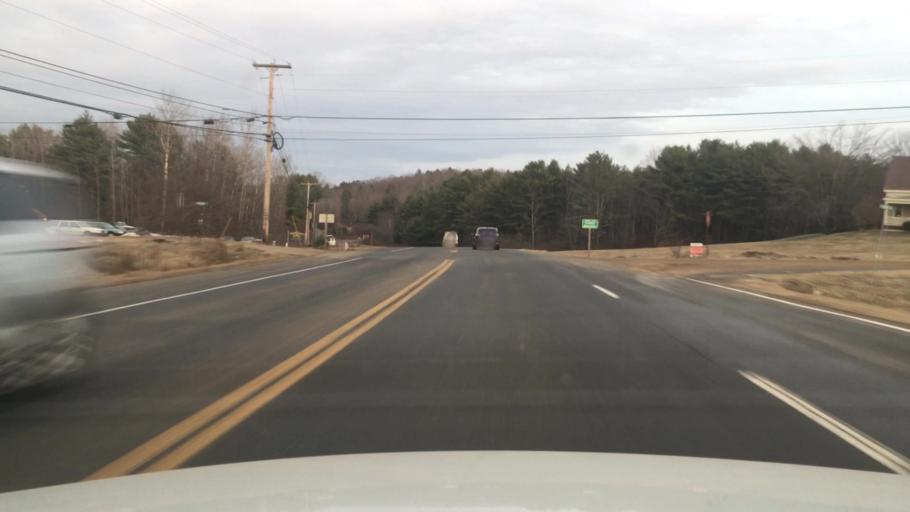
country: US
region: Maine
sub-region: Lincoln County
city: Edgecomb
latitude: 44.0029
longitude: -69.6125
